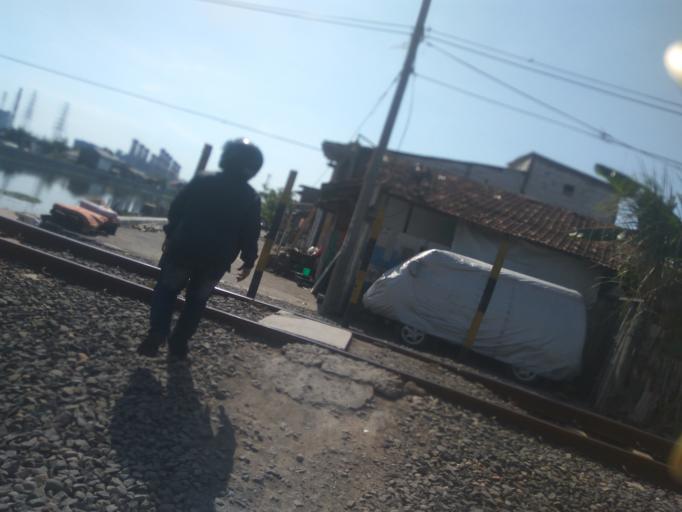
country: ID
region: Central Java
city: Semarang
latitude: -6.9557
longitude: 110.4392
